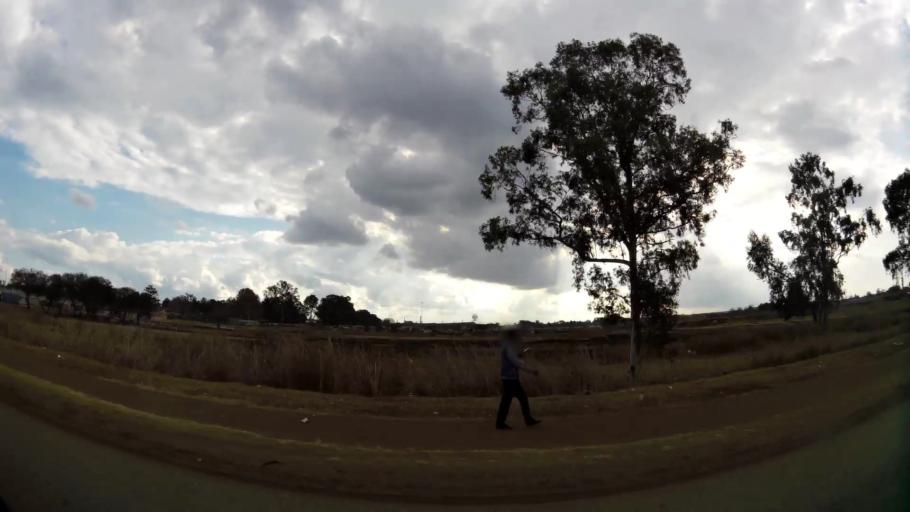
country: ZA
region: Gauteng
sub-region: Sedibeng District Municipality
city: Vanderbijlpark
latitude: -26.6707
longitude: 27.8484
